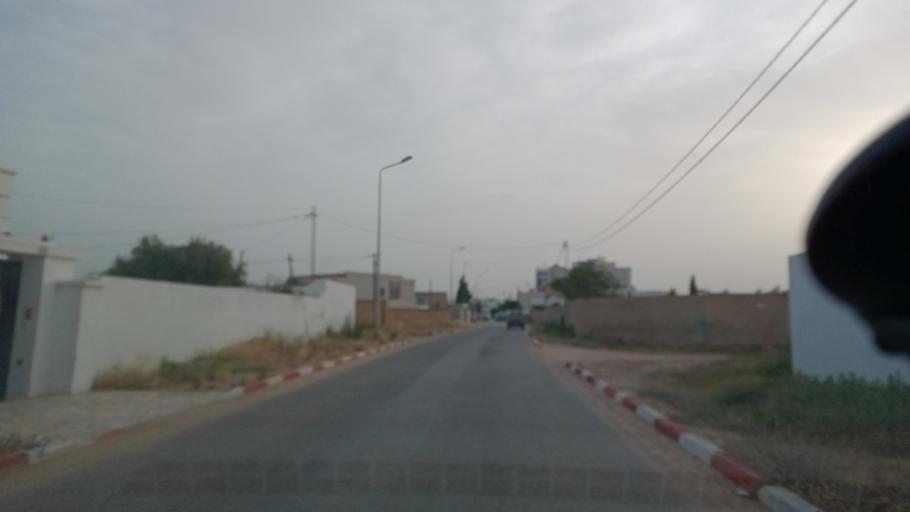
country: TN
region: Safaqis
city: Al Qarmadah
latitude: 34.7831
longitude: 10.7635
